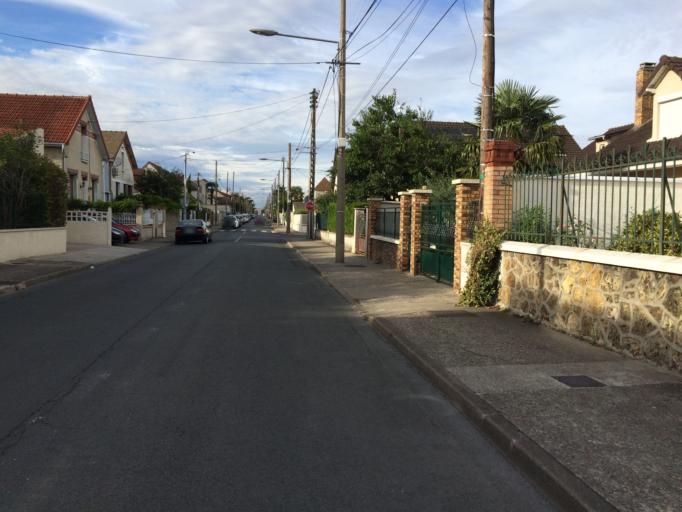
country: FR
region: Ile-de-France
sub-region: Departement de l'Essonne
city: Paray-Vieille-Poste
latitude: 48.7073
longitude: 2.3540
